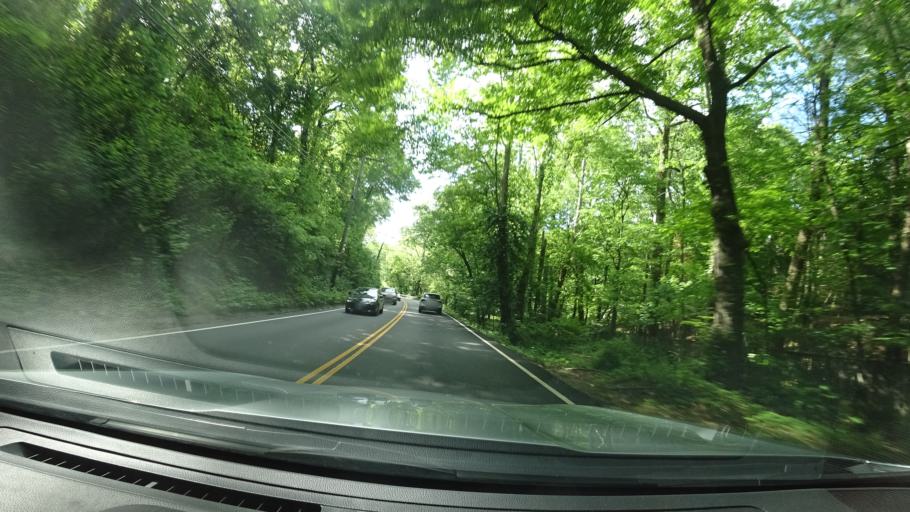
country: US
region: Virginia
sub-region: Fairfax County
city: McLean
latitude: 38.9284
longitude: -77.1673
